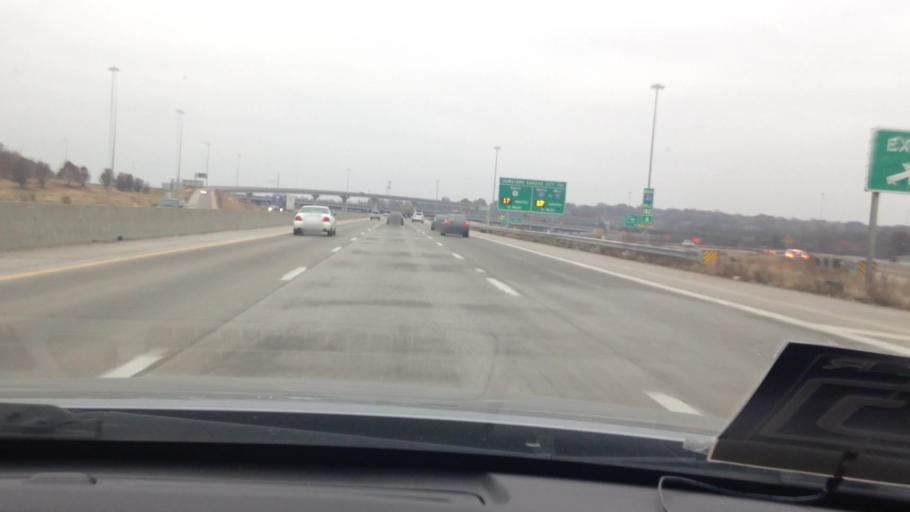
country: US
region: Missouri
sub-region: Jackson County
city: Grandview
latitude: 38.9259
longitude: -94.5275
